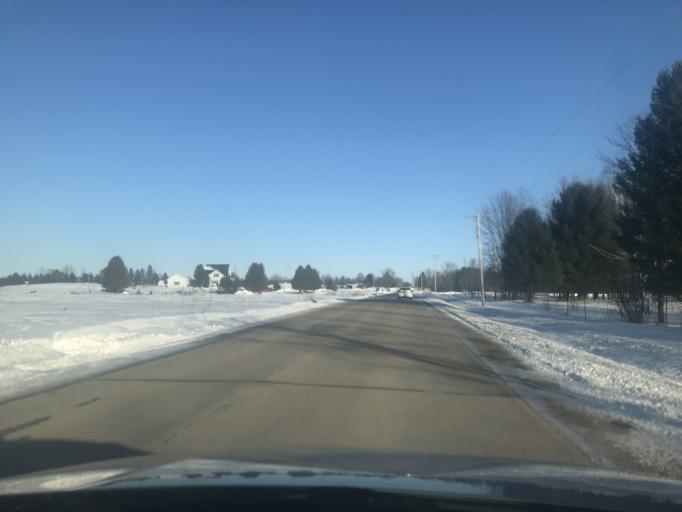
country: US
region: Wisconsin
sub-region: Marinette County
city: Marinette
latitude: 45.1450
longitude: -87.6633
